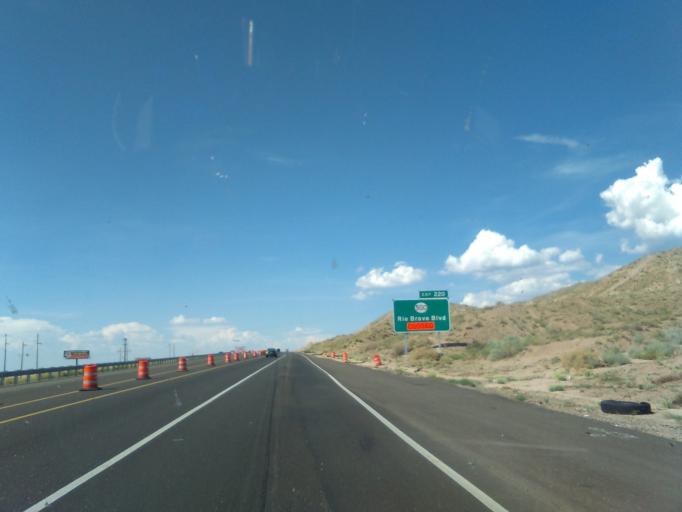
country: US
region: New Mexico
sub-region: Bernalillo County
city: South Valley
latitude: 35.0127
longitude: -106.6407
